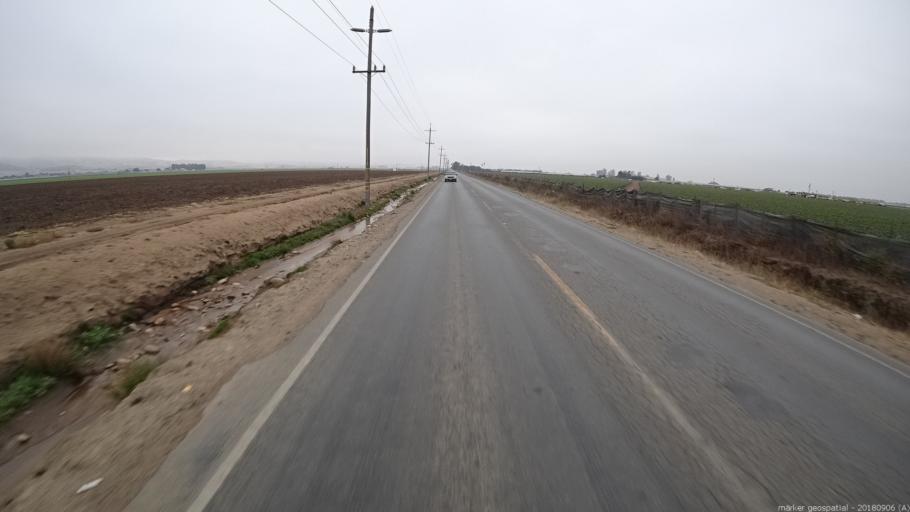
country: US
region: California
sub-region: Monterey County
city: Chualar
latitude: 36.6295
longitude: -121.5386
